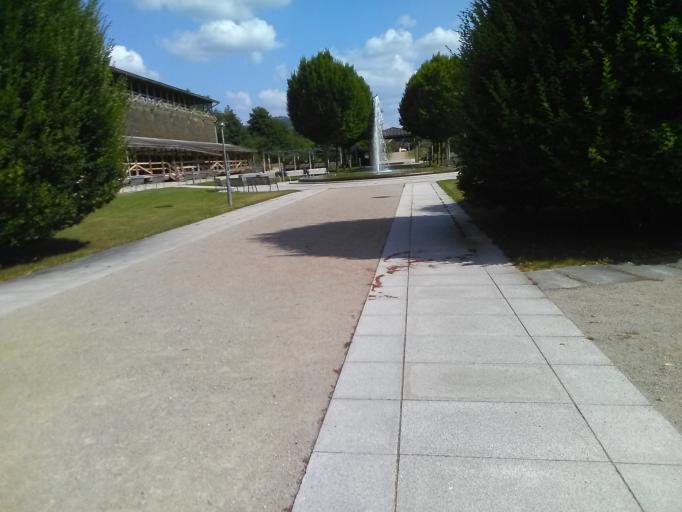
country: DE
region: Bavaria
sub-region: Upper Franconia
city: Bad Staffelstein
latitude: 50.1104
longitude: 10.9874
